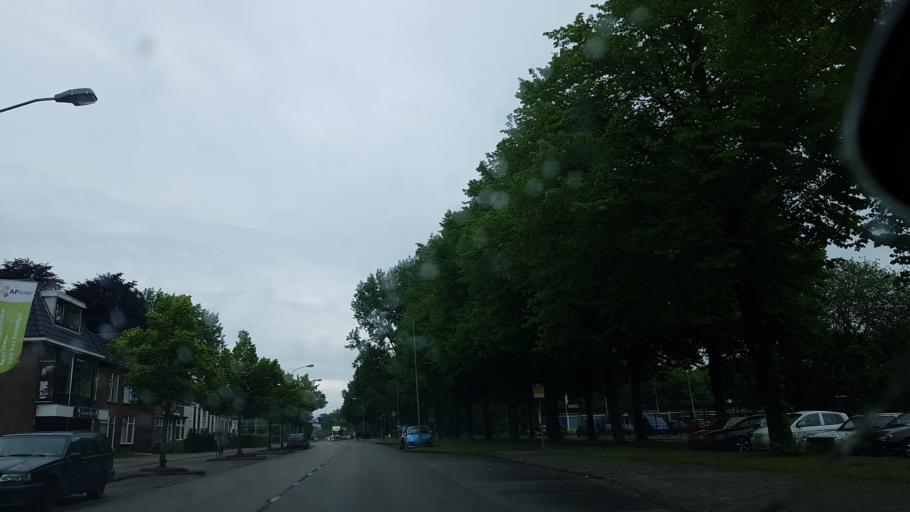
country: NL
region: Groningen
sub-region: Gemeente Hoogezand-Sappemeer
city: Hoogezand
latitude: 53.1634
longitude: 6.7495
